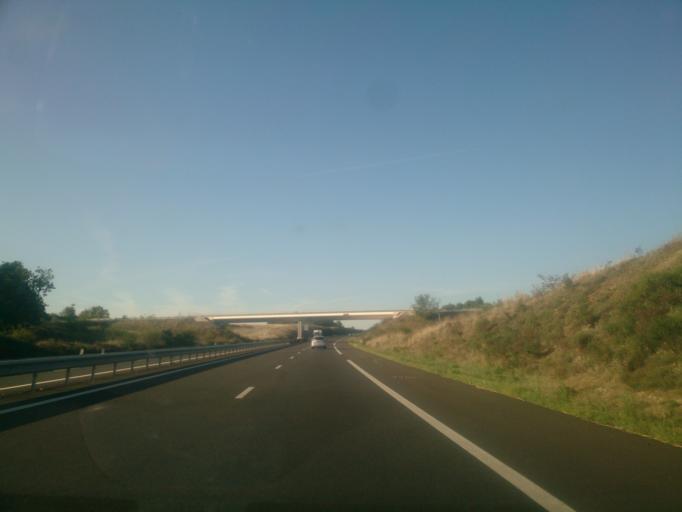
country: FR
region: Midi-Pyrenees
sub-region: Departement du Lot
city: Pradines
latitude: 44.5727
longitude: 1.5125
